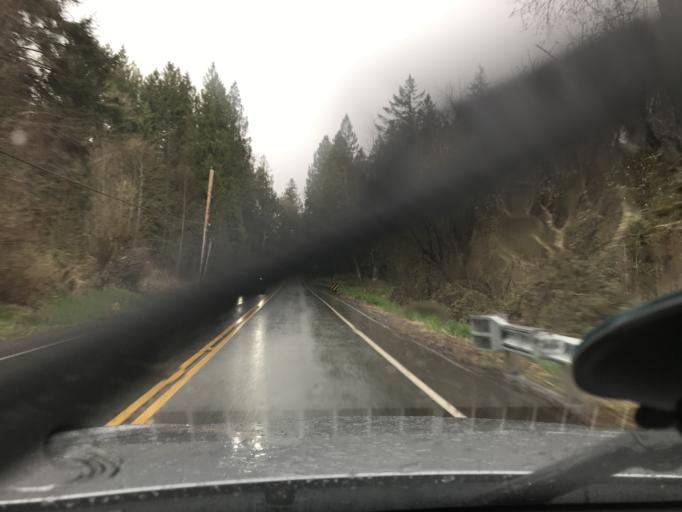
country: US
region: Washington
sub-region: King County
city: Ames Lake
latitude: 47.6620
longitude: -121.9689
